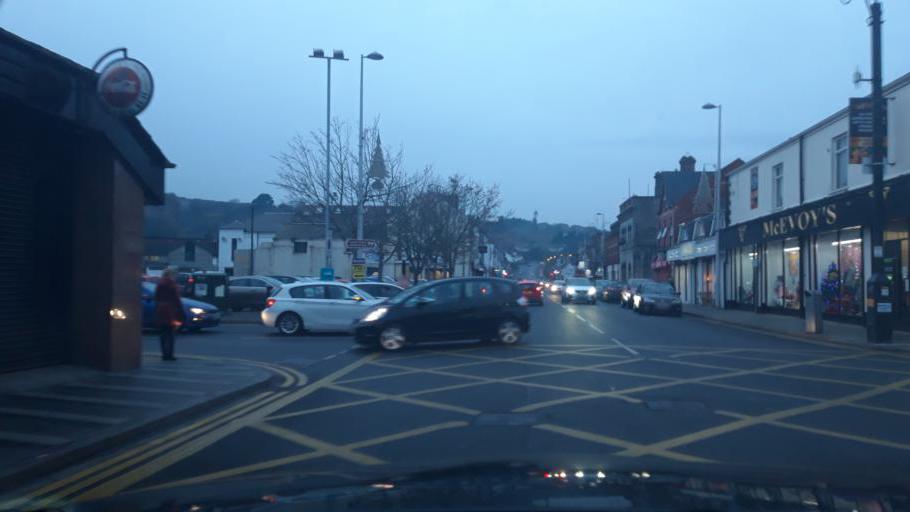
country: GB
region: Northern Ireland
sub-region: Newry and Mourne District
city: Newry
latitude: 54.1769
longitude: -6.3416
